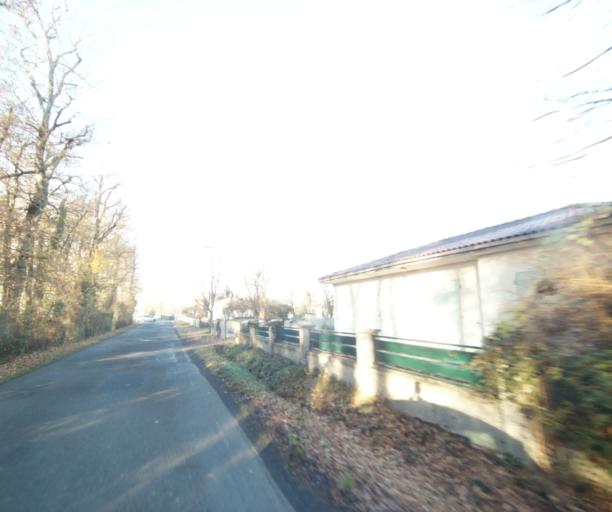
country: FR
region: Poitou-Charentes
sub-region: Departement de la Charente-Maritime
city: Bussac-sur-Charente
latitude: 45.7668
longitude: -0.6145
